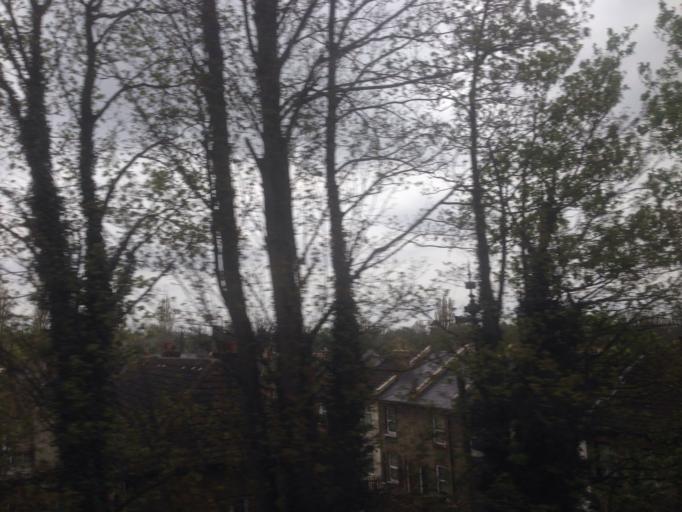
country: GB
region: England
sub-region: Greater London
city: Carshalton
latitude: 51.3694
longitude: -0.1633
